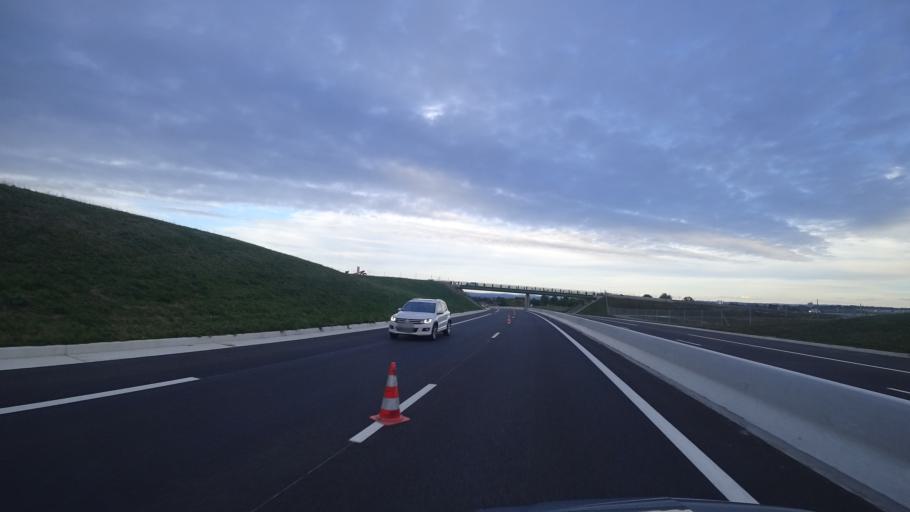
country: FR
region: Midi-Pyrenees
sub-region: Departement de l'Aveyron
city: Luc-la-Primaube
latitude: 44.2905
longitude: 2.5088
